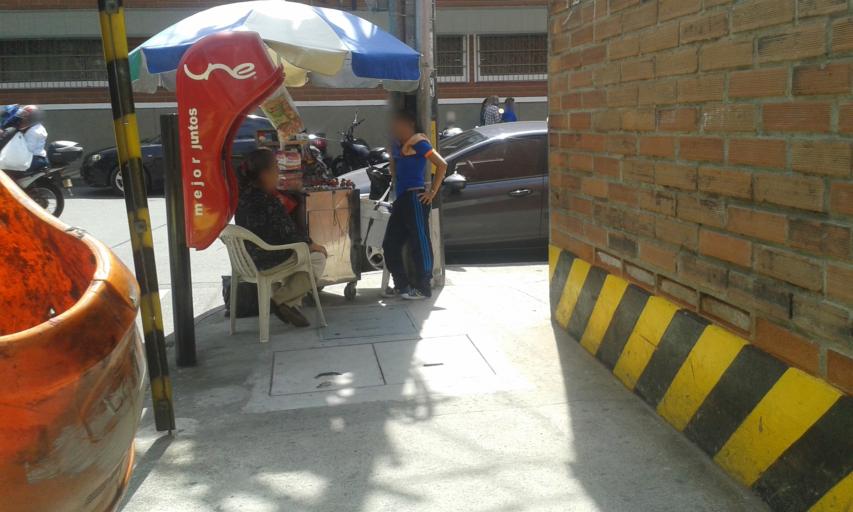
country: CO
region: Antioquia
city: Medellin
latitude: 6.2513
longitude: -75.5730
